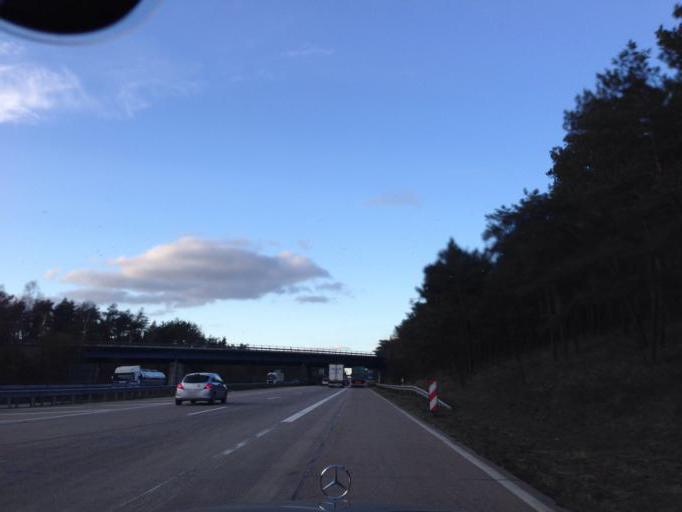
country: DE
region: Lower Saxony
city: Bad Fallingbostel
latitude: 52.7877
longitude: 9.6725
